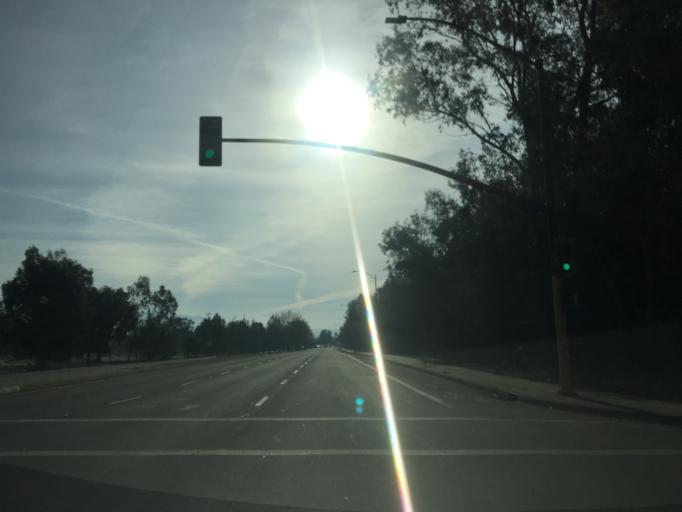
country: US
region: California
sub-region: Santa Clara County
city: Alum Rock
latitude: 37.3393
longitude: -121.8040
